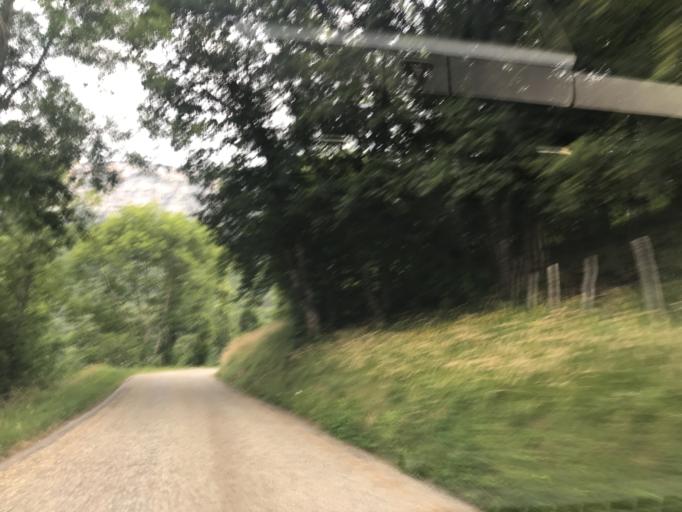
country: FR
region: Rhone-Alpes
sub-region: Departement de l'Isere
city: Saint-Vincent-de-Mercuze
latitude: 45.3957
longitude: 5.9421
